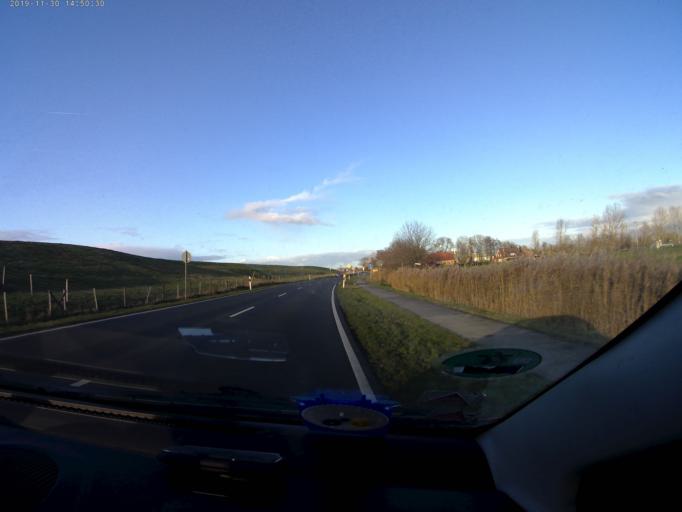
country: DE
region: Lower Saxony
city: Jemgum
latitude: 53.2594
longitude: 7.4059
